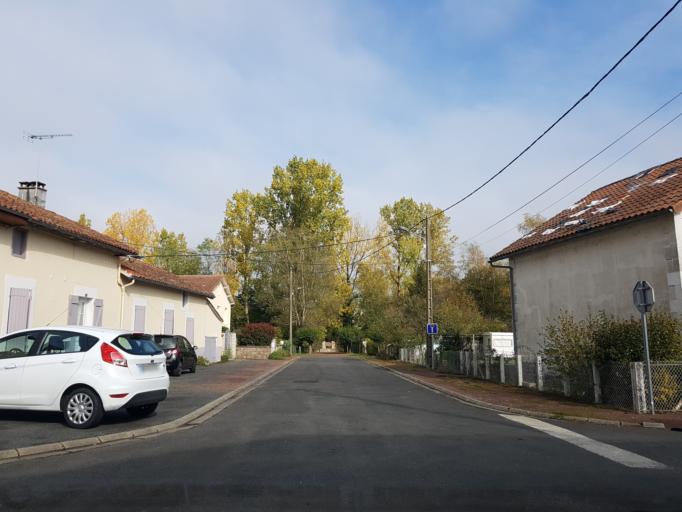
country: FR
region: Poitou-Charentes
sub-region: Departement de la Charente
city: Chabanais
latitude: 45.8749
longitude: 0.7132
